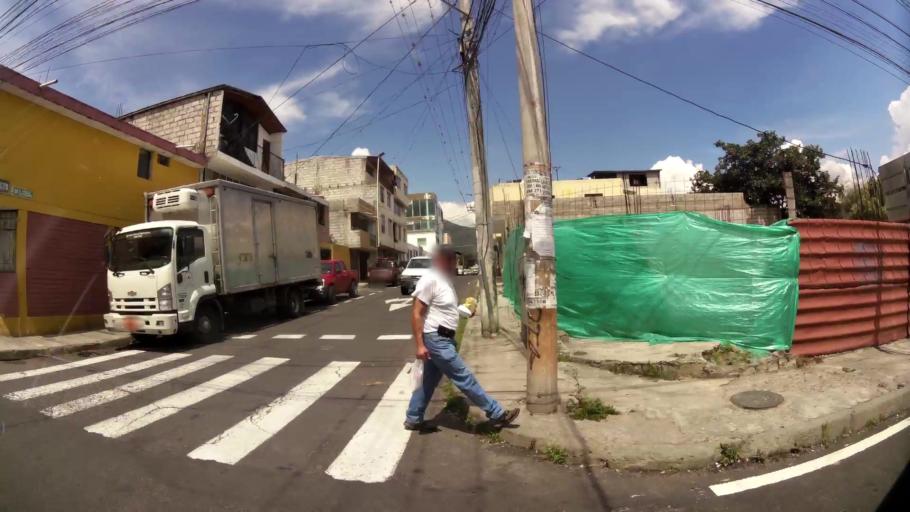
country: EC
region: Pichincha
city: Quito
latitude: -0.2122
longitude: -78.4060
